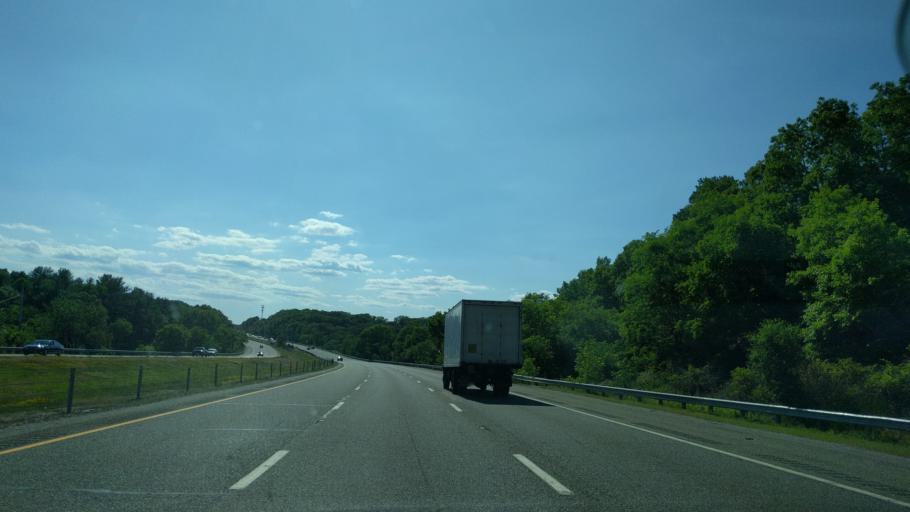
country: US
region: Rhode Island
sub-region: Providence County
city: Valley Falls
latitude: 41.9533
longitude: -71.3821
